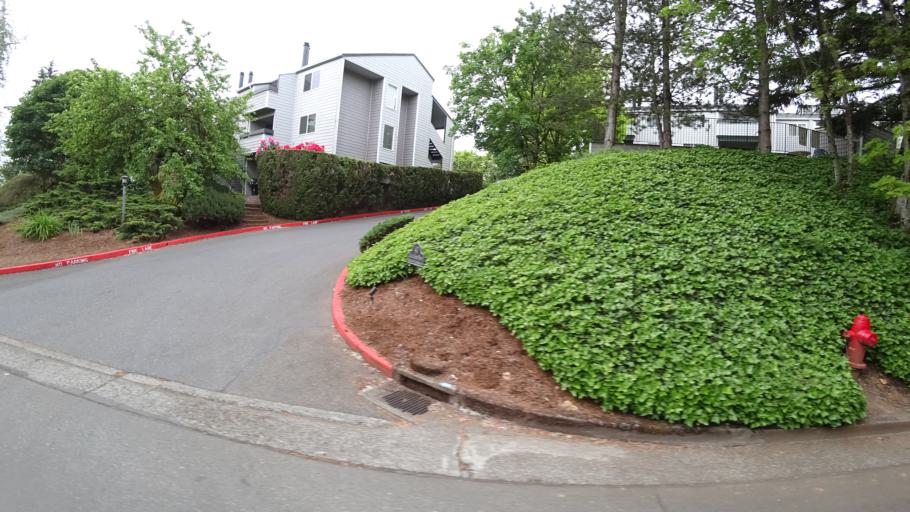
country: US
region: Oregon
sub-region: Clackamas County
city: Lake Oswego
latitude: 45.4369
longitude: -122.7092
